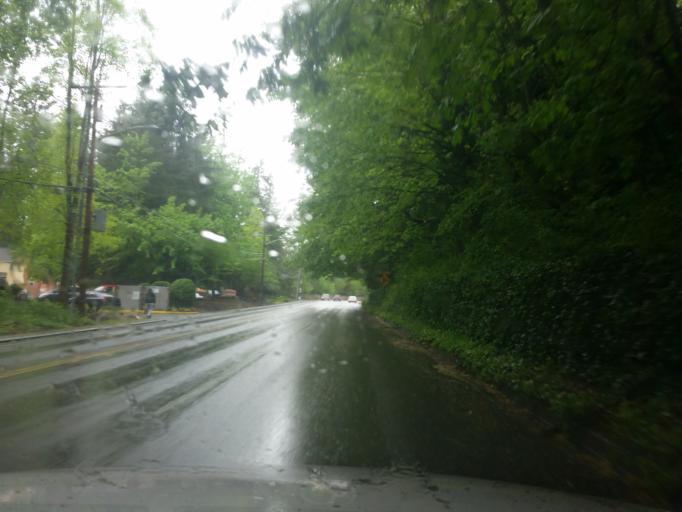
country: US
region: Washington
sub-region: King County
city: Inglewood-Finn Hill
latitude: 47.7330
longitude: -122.2148
